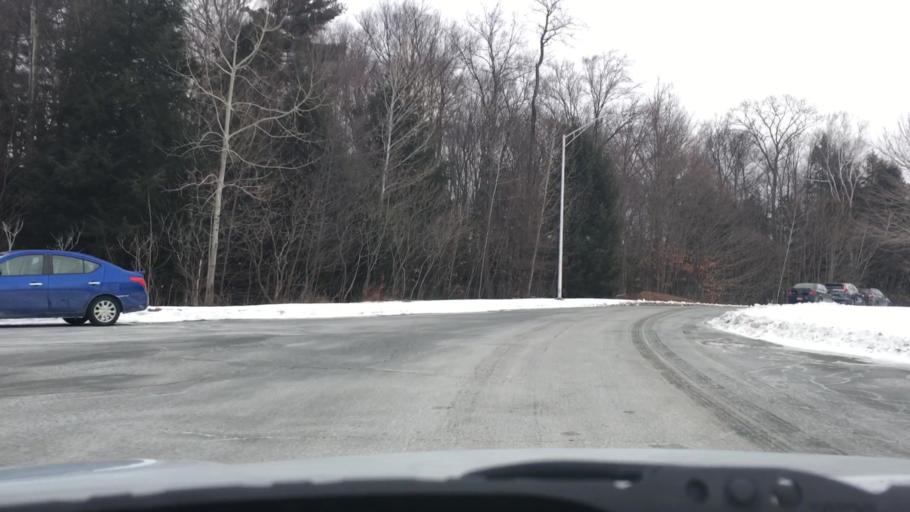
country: US
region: Massachusetts
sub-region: Berkshire County
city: Pittsfield
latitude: 42.4139
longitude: -73.2707
